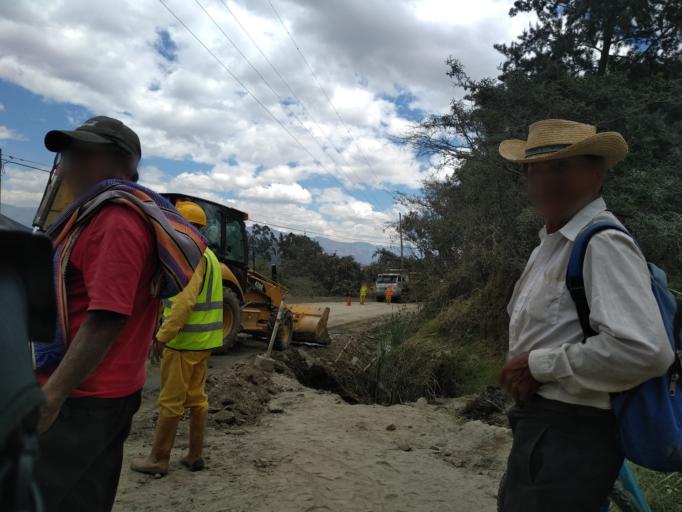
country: EC
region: Loja
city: Loja
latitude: -4.2122
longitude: -79.2395
